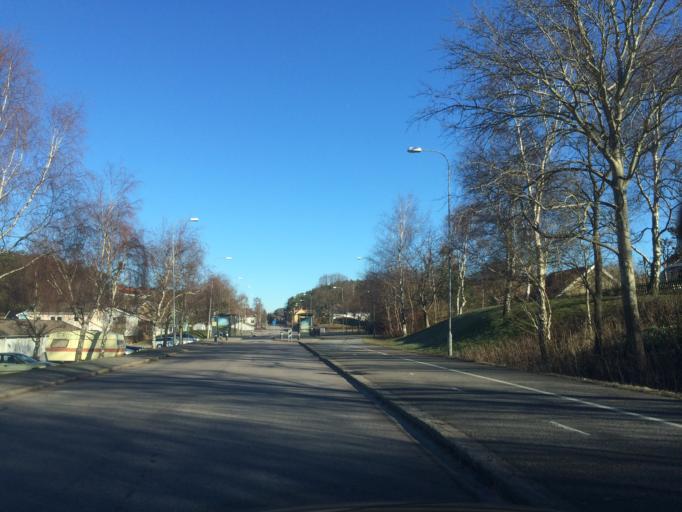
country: SE
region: Vaestra Goetaland
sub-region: Goteborg
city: Majorna
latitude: 57.6642
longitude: 11.8973
